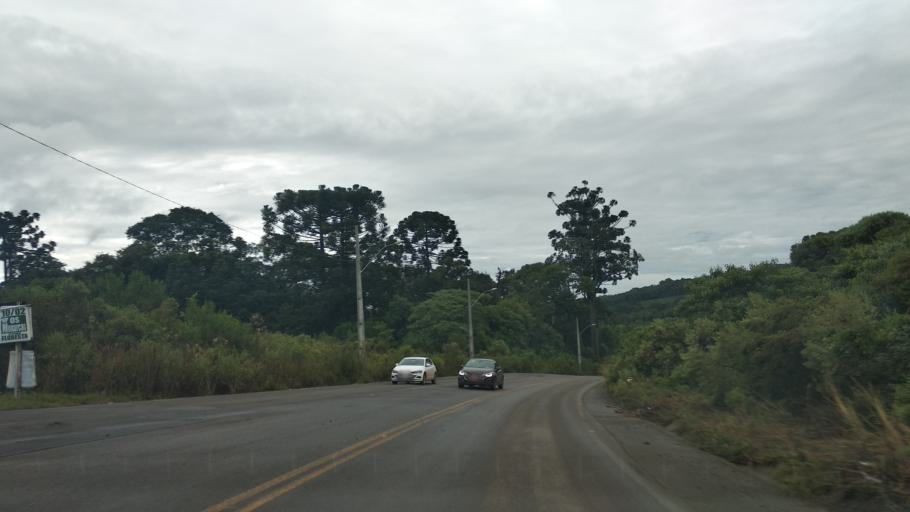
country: BR
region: Santa Catarina
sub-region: Videira
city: Videira
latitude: -27.0303
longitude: -51.1569
